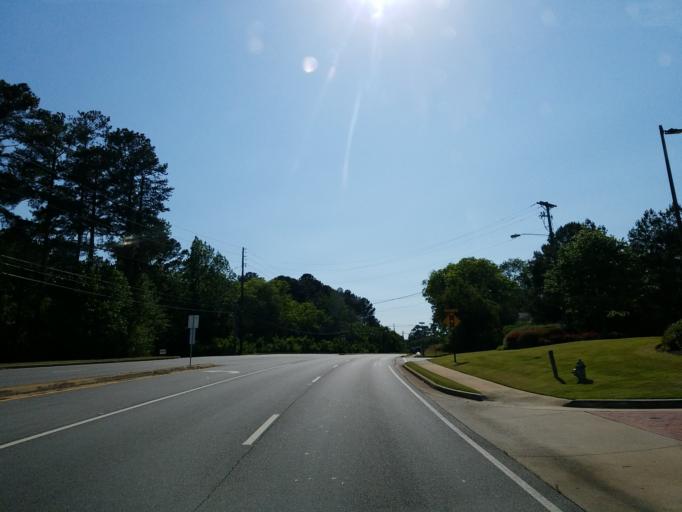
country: US
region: Georgia
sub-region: Cobb County
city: Marietta
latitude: 34.0193
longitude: -84.5309
